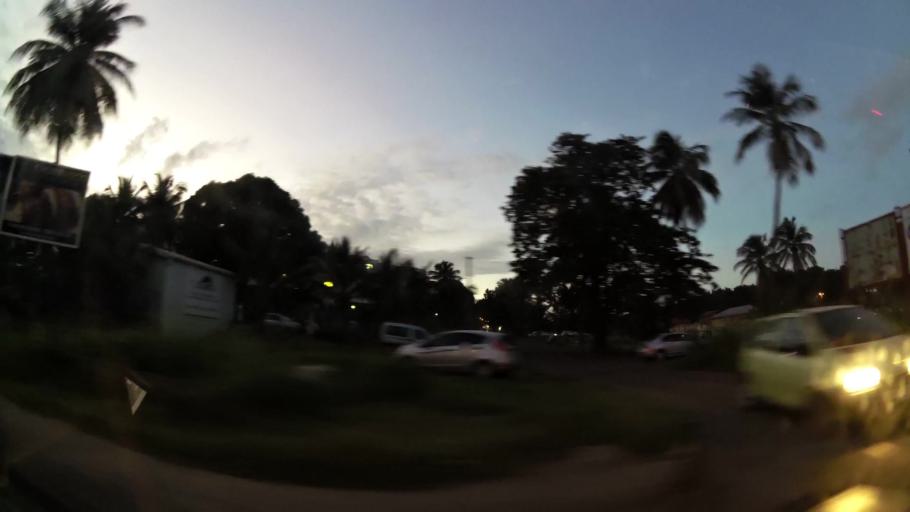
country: GP
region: Guadeloupe
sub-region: Guadeloupe
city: Pointe-a-Pitre
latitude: 16.2559
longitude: -61.5214
